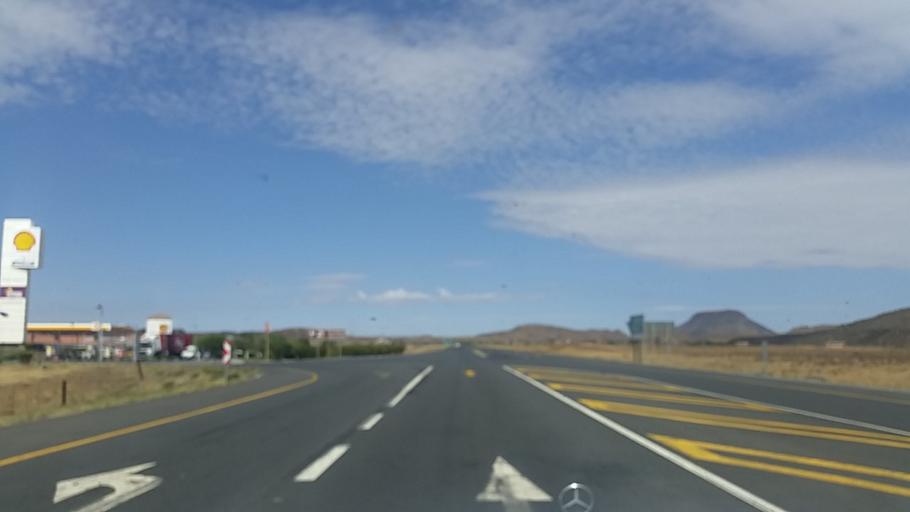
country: ZA
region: Northern Cape
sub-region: Pixley ka Seme District Municipality
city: Colesberg
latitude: -30.6998
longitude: 25.1271
